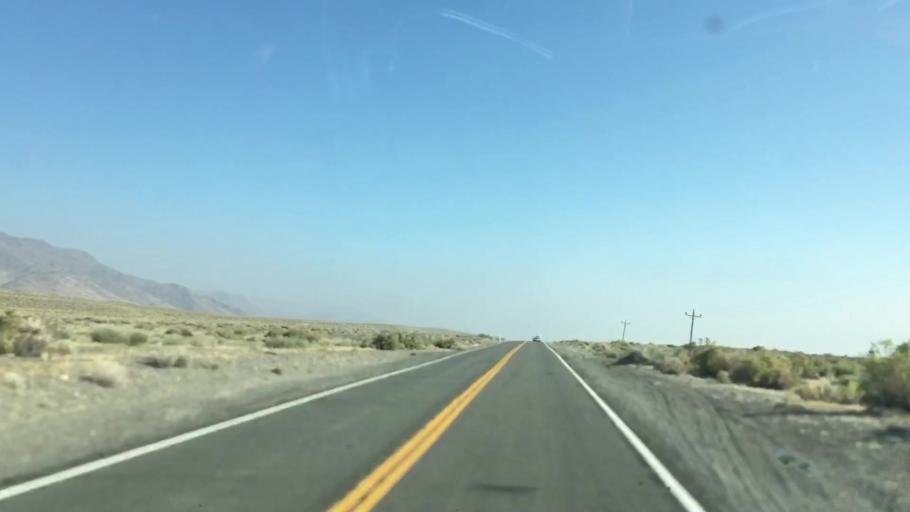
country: US
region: Nevada
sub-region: Lyon County
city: Fernley
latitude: 40.1512
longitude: -119.3680
